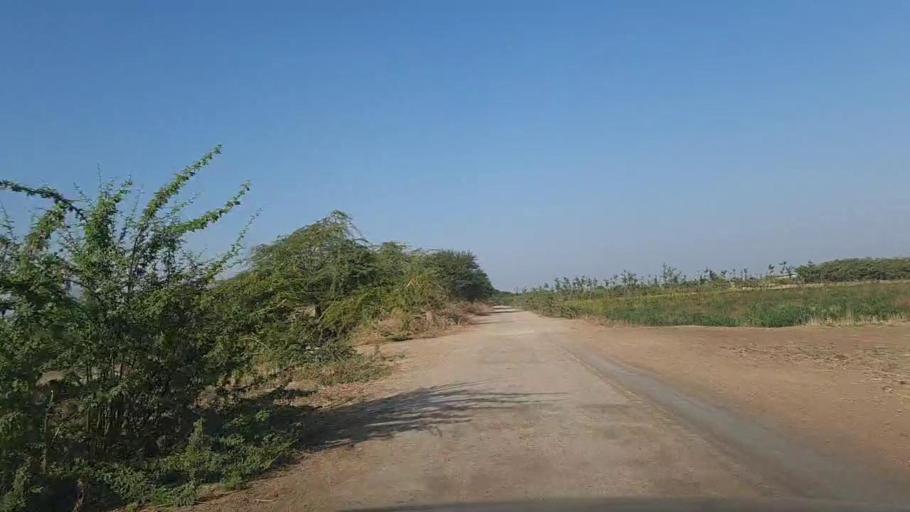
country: PK
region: Sindh
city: Digri
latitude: 25.0386
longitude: 69.2651
